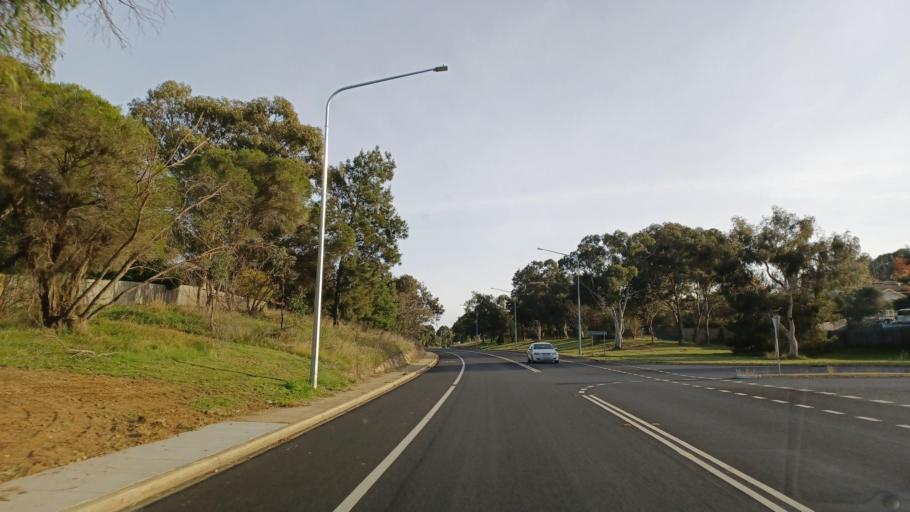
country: AU
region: Australian Capital Territory
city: Belconnen
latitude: -35.1998
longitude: 149.0623
